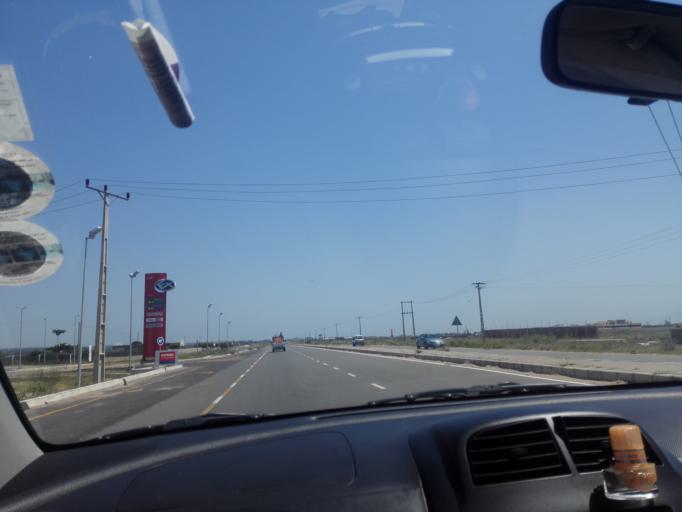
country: MZ
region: Maputo City
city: Maputo
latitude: -25.8429
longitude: 32.6715
